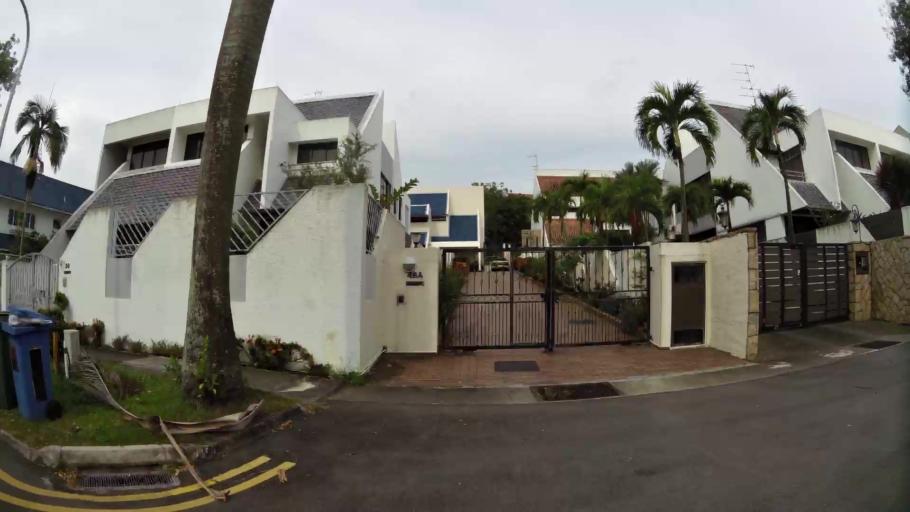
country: SG
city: Singapore
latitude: 1.3236
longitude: 103.7943
